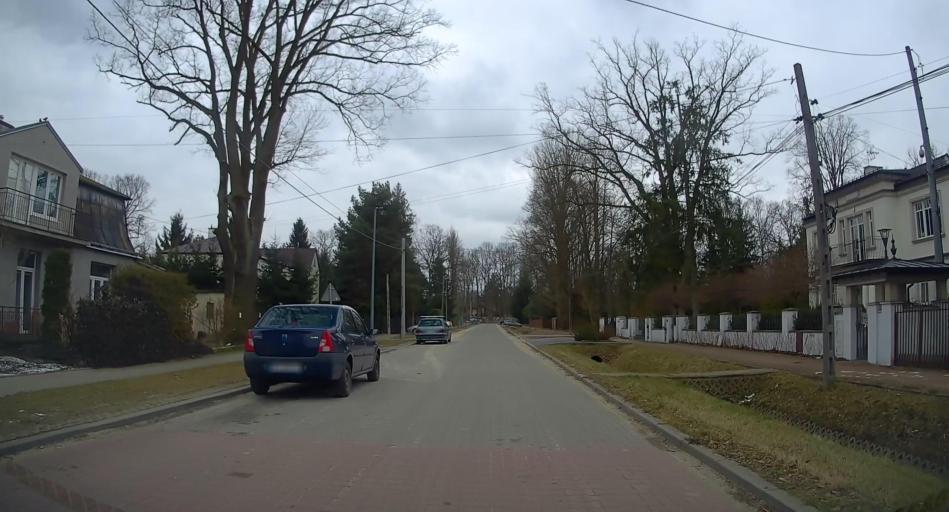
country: PL
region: Masovian Voivodeship
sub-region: Powiat piaseczynski
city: Piaseczno
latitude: 52.0605
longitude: 21.0015
